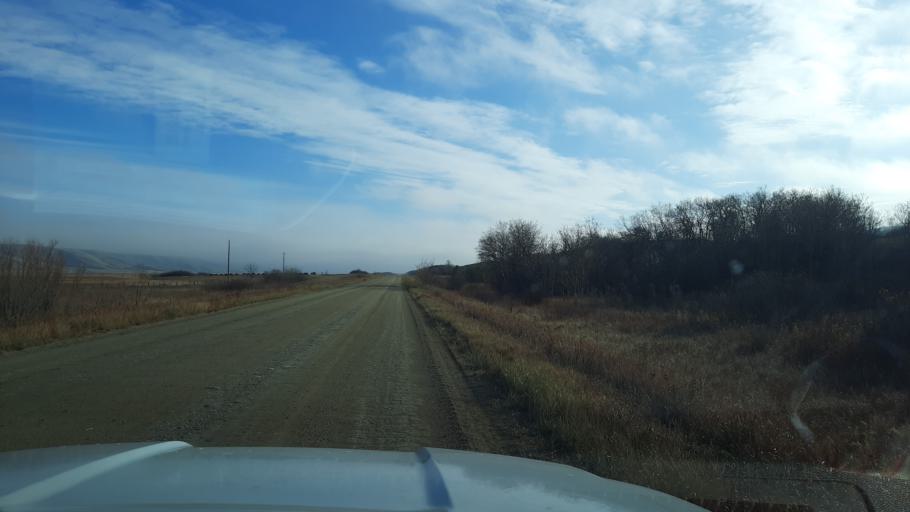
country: CA
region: Saskatchewan
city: Pilot Butte
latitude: 50.7835
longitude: -104.2509
